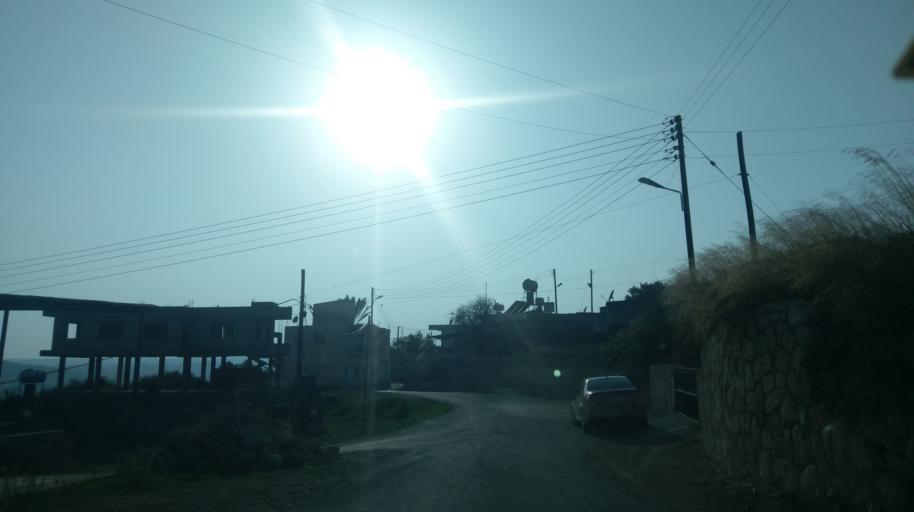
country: CY
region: Ammochostos
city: Leonarisso
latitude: 35.4799
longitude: 34.1093
